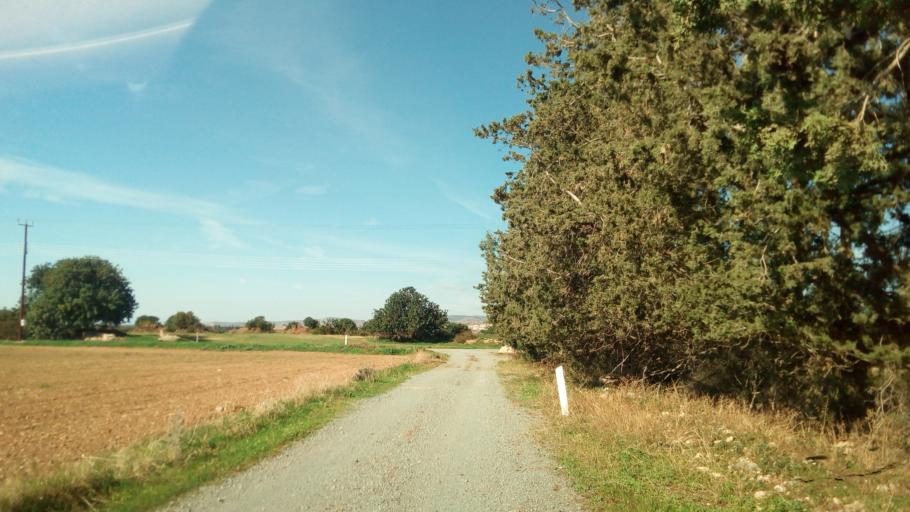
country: CY
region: Limassol
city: Pissouri
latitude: 34.7146
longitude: 32.5887
